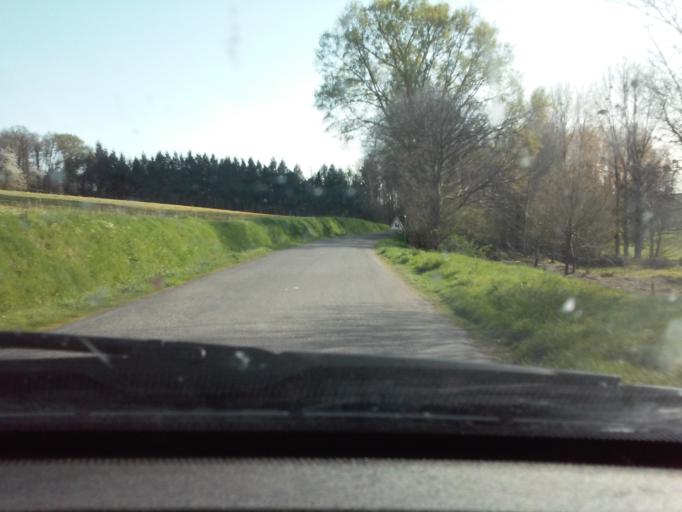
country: FR
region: Brittany
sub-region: Departement d'Ille-et-Vilaine
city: Javene
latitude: 48.3129
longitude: -1.2444
